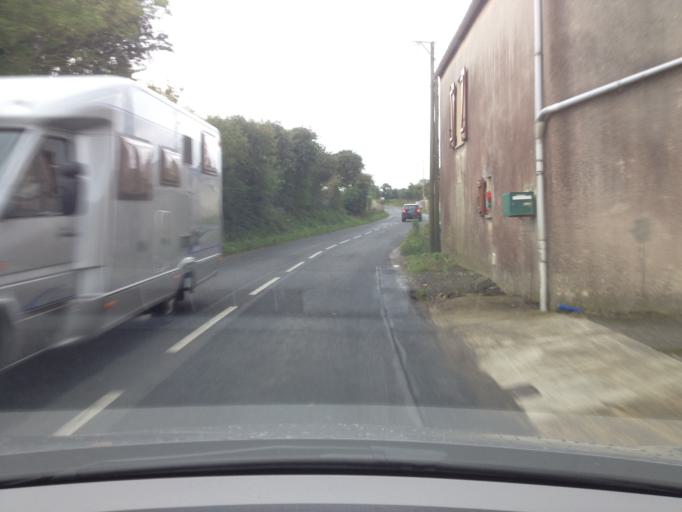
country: FR
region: Lower Normandy
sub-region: Departement du Calvados
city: Grandcamp-Maisy
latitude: 49.3912
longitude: -1.0011
